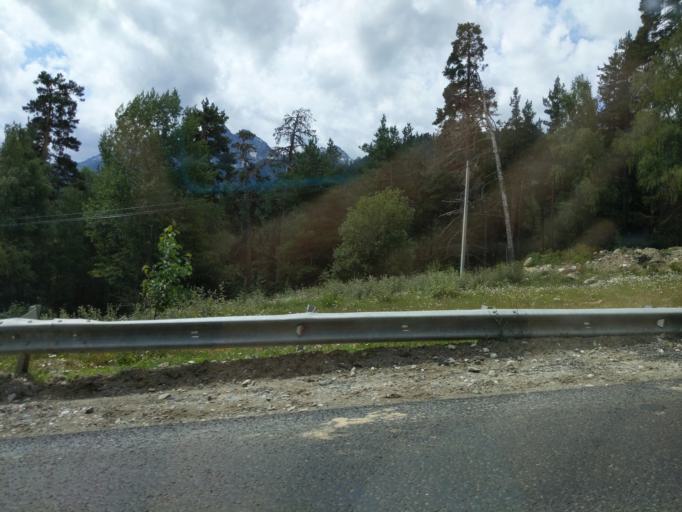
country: RU
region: Karachayevo-Cherkesiya
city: Nizhniy Arkhyz
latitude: 43.5370
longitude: 41.2158
